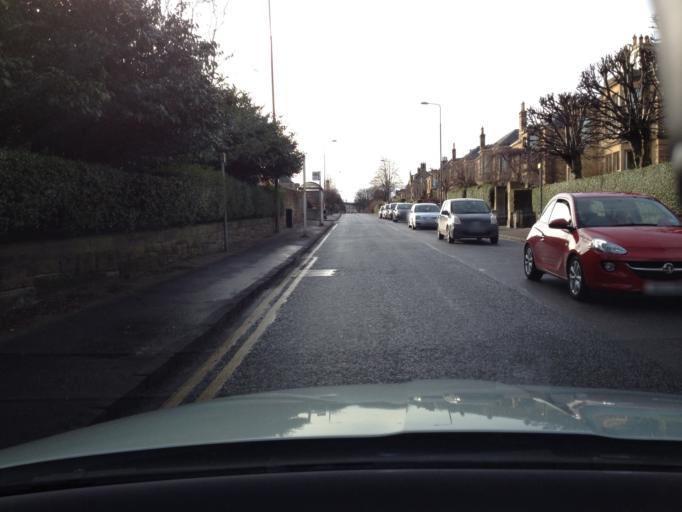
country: GB
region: Scotland
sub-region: Edinburgh
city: Edinburgh
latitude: 55.9259
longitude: -3.1672
